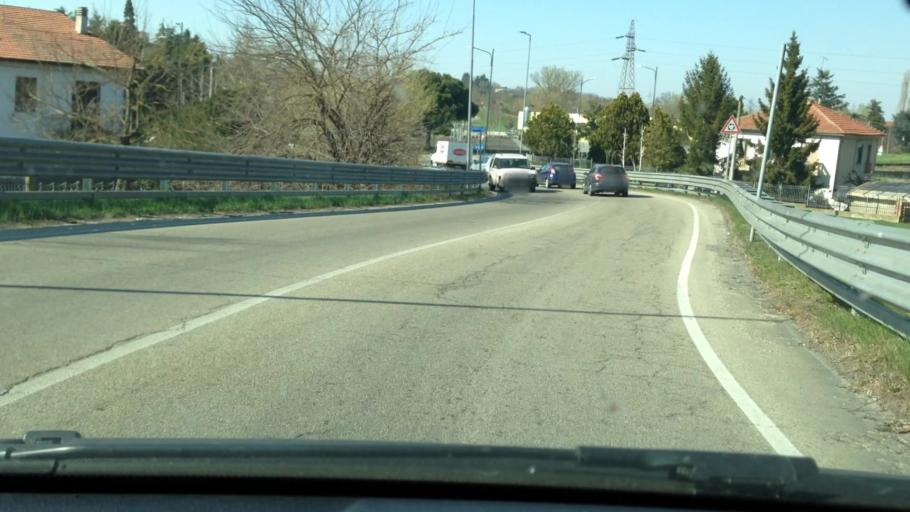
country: IT
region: Piedmont
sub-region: Provincia di Asti
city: Asti
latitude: 44.9191
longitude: 8.2263
